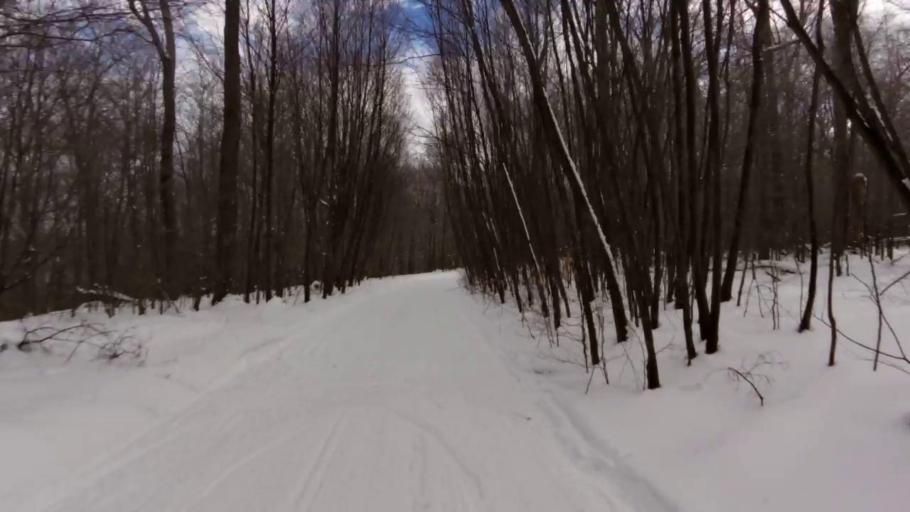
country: US
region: Pennsylvania
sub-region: McKean County
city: Bradford
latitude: 42.0056
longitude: -78.6736
